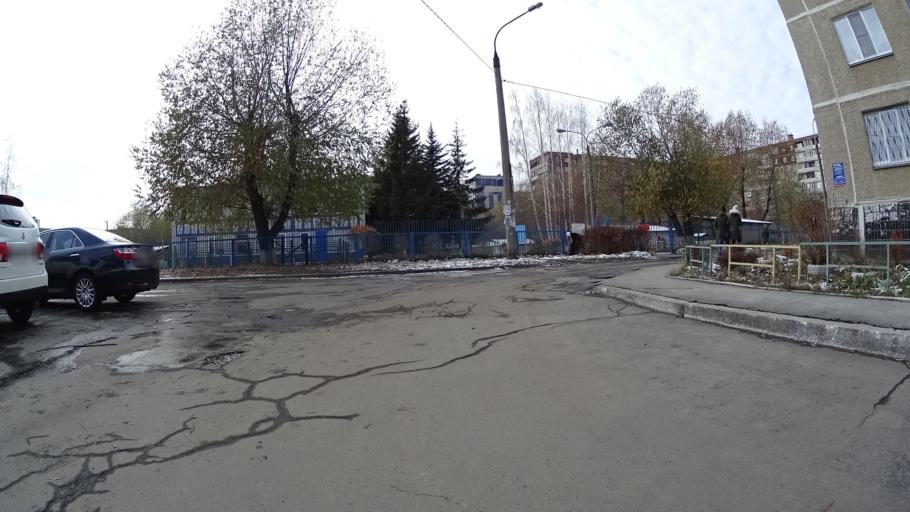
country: RU
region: Chelyabinsk
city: Roshchino
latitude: 55.1902
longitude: 61.2984
